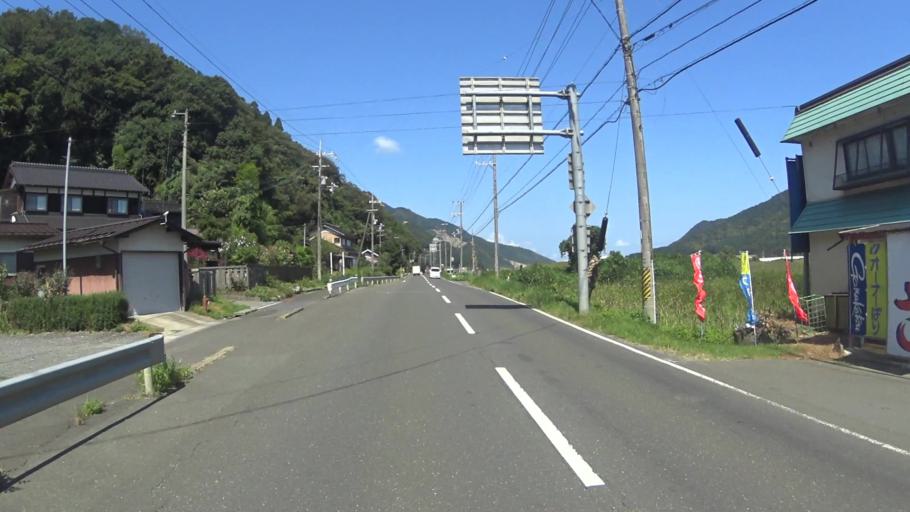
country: JP
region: Kyoto
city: Maizuru
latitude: 35.4663
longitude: 135.2781
